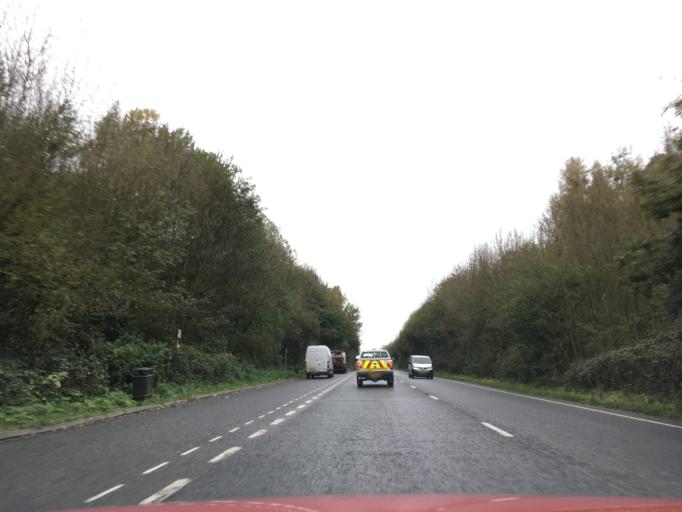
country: GB
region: England
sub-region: Hampshire
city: Eastleigh
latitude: 50.9921
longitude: -1.3533
